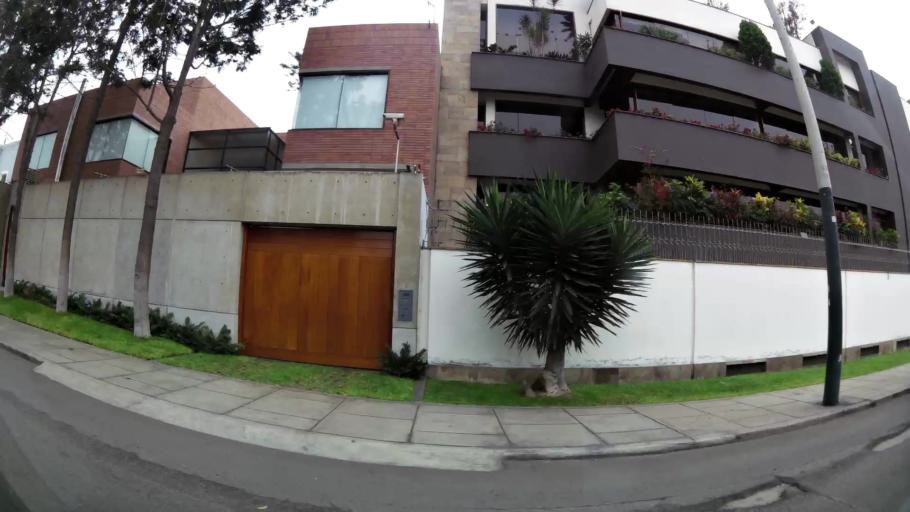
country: PE
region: Lima
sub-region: Lima
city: San Isidro
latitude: -12.0976
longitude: -77.0430
